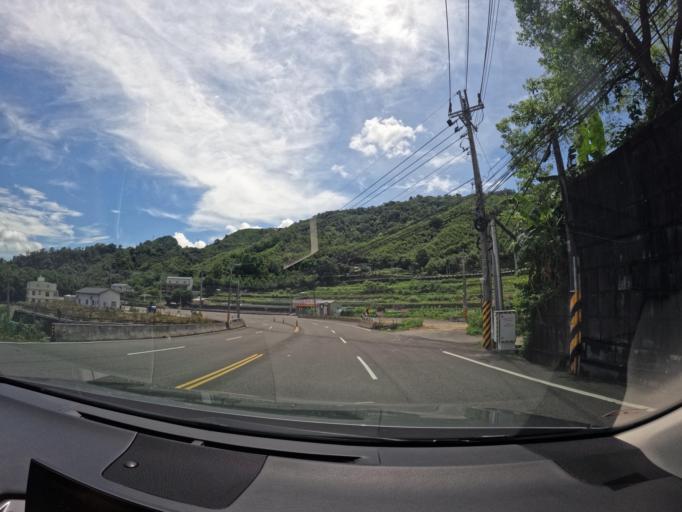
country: TW
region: Taiwan
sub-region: Miaoli
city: Miaoli
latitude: 24.4579
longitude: 120.8828
